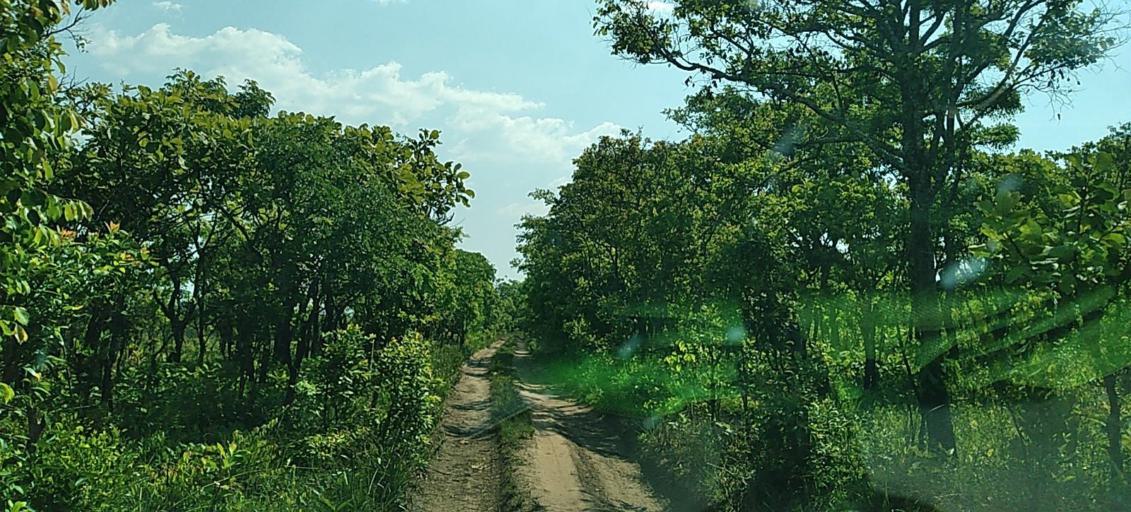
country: CD
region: Katanga
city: Kolwezi
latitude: -11.2669
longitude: 24.9985
